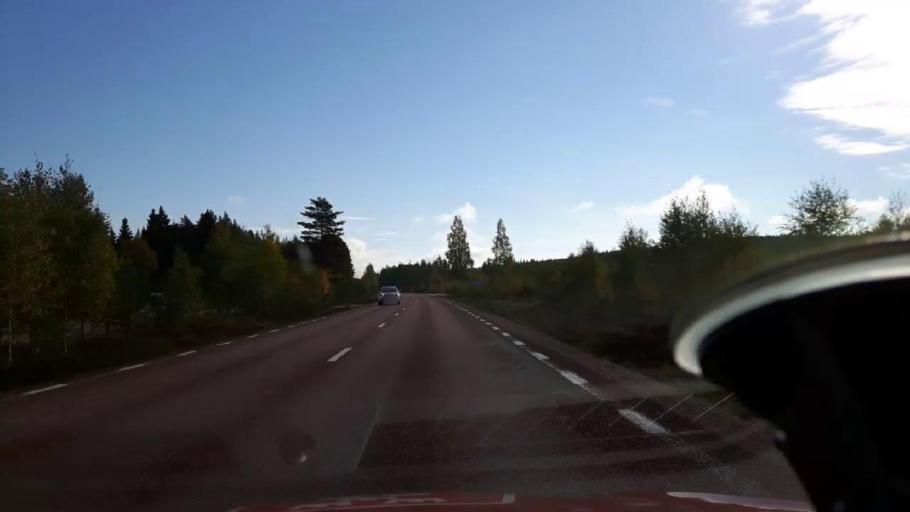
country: SE
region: Gaevleborg
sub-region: Ljusdals Kommun
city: Farila
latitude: 61.9319
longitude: 15.5365
